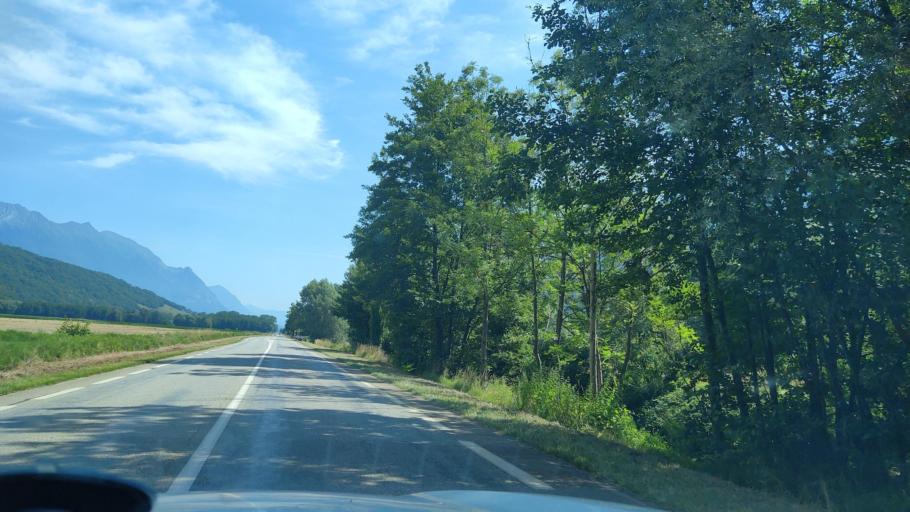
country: FR
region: Rhone-Alpes
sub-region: Departement de la Savoie
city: Coise-Saint-Jean-Pied-Gauthier
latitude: 45.4949
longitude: 6.1573
